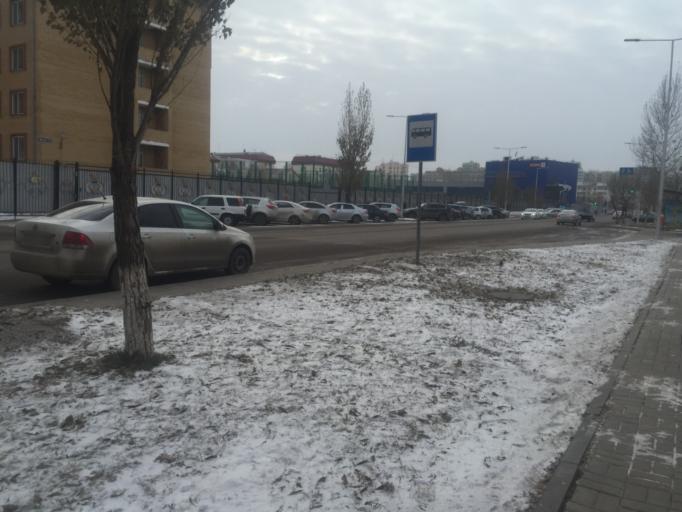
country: KZ
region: Astana Qalasy
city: Astana
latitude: 51.1822
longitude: 71.4144
